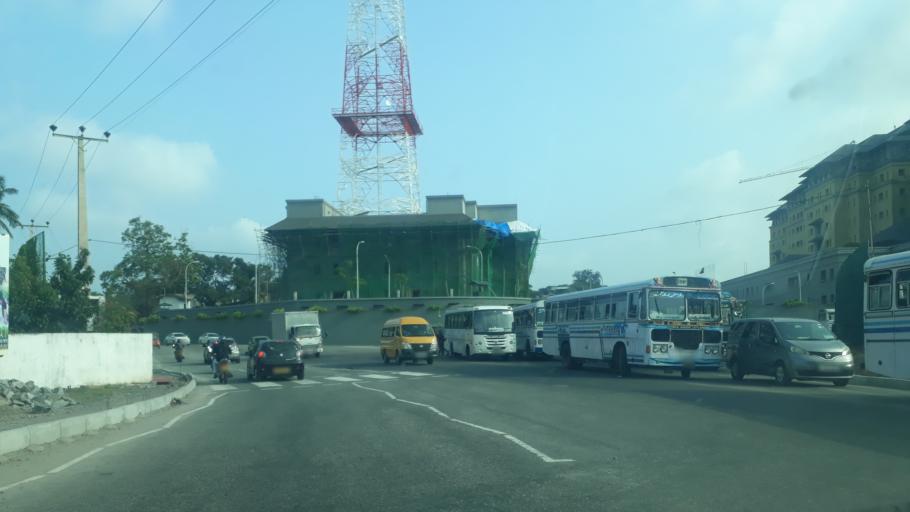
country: LK
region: Western
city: Battaramulla South
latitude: 6.8936
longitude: 79.9375
